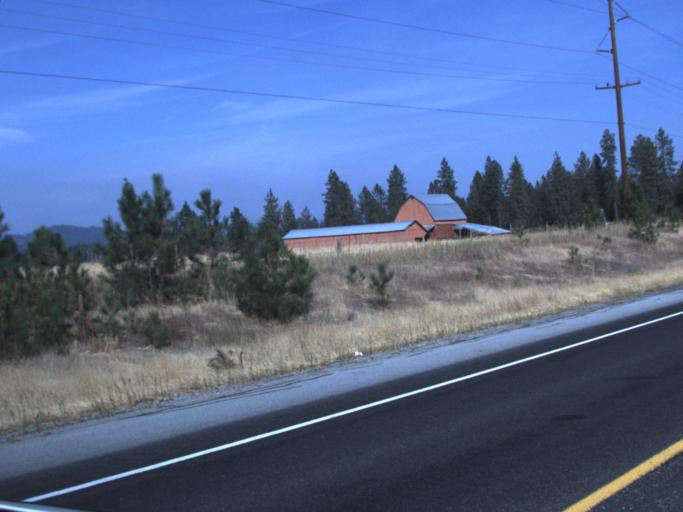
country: US
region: Washington
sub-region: Pend Oreille County
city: Newport
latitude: 48.0973
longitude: -117.2667
